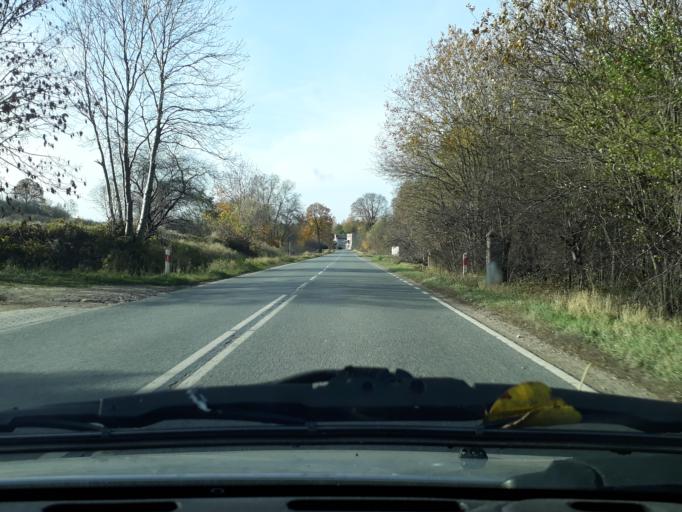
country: PL
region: Silesian Voivodeship
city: Wozniki
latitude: 50.5915
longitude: 19.0734
